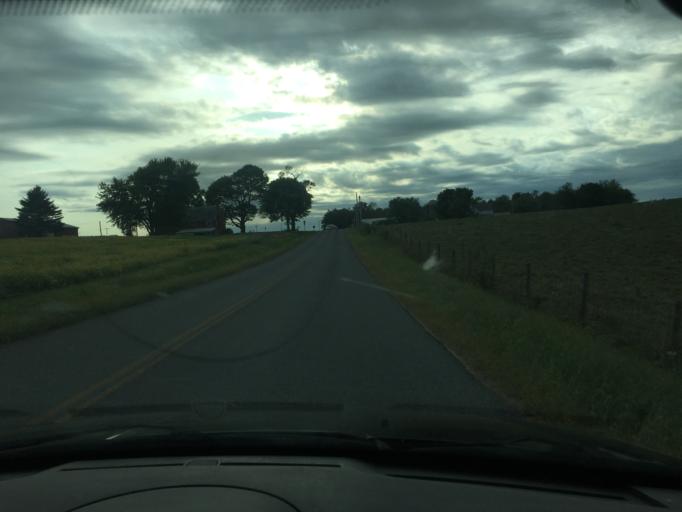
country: US
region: Ohio
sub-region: Logan County
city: West Liberty
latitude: 40.2706
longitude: -83.7203
